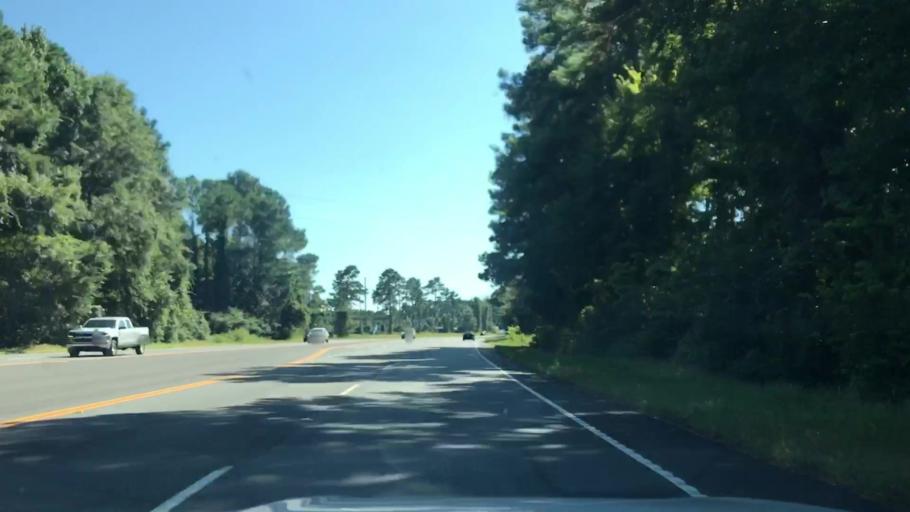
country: US
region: South Carolina
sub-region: Charleston County
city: Awendaw
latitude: 33.1011
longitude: -79.4679
